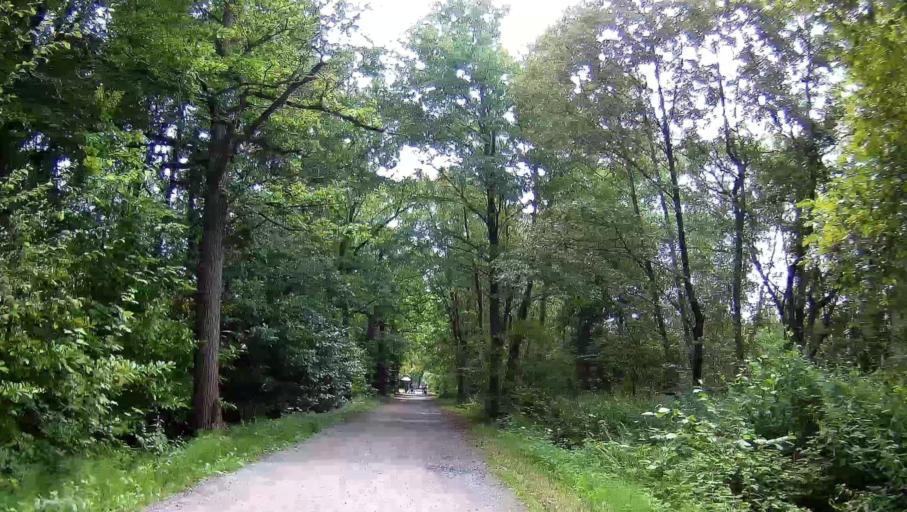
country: BE
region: Flanders
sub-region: Provincie Antwerpen
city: Balen
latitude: 51.2123
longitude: 5.2034
